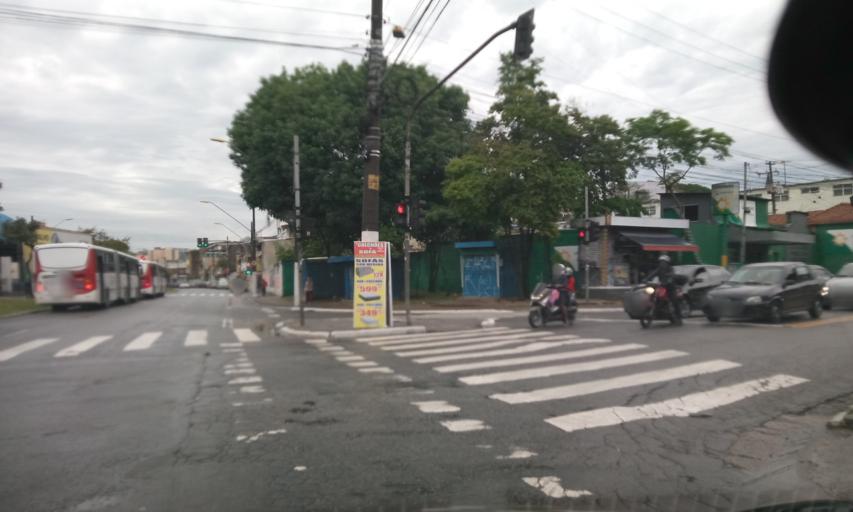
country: BR
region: Sao Paulo
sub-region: Santo Andre
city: Santo Andre
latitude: -23.6984
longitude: -46.5062
